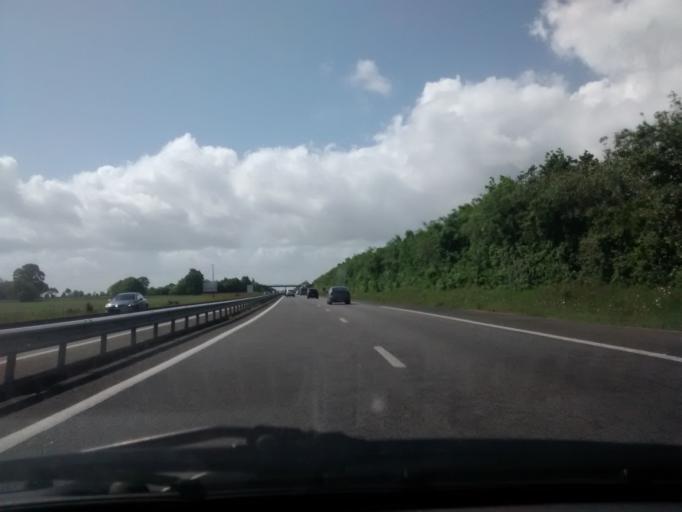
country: FR
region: Brittany
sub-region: Departement d'Ille-et-Vilaine
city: Plelan-le-Grand
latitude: 47.9932
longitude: -2.0979
